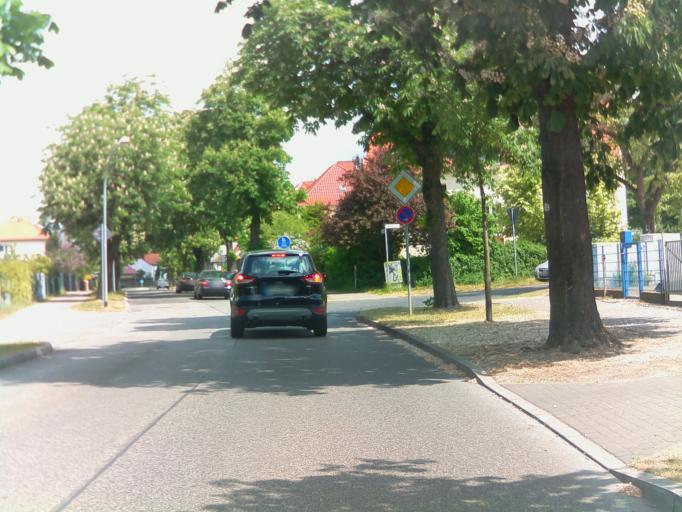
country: DE
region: Brandenburg
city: Dallgow-Doeberitz
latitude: 52.5527
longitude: 13.0711
